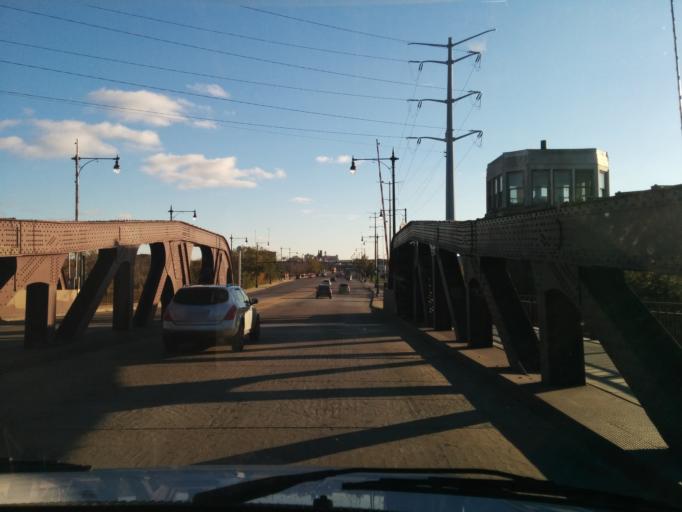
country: US
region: Illinois
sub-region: Cook County
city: Chicago
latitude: 41.8449
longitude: -87.6660
